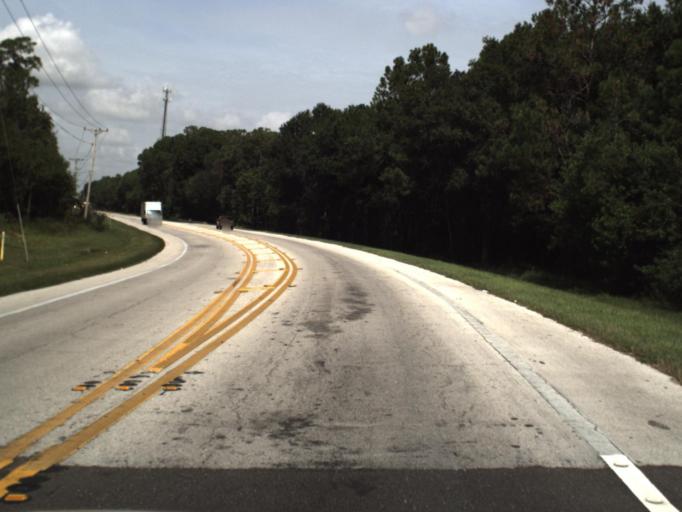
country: US
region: Florida
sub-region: Polk County
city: Jan-Phyl Village
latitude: 28.0133
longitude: -81.7523
